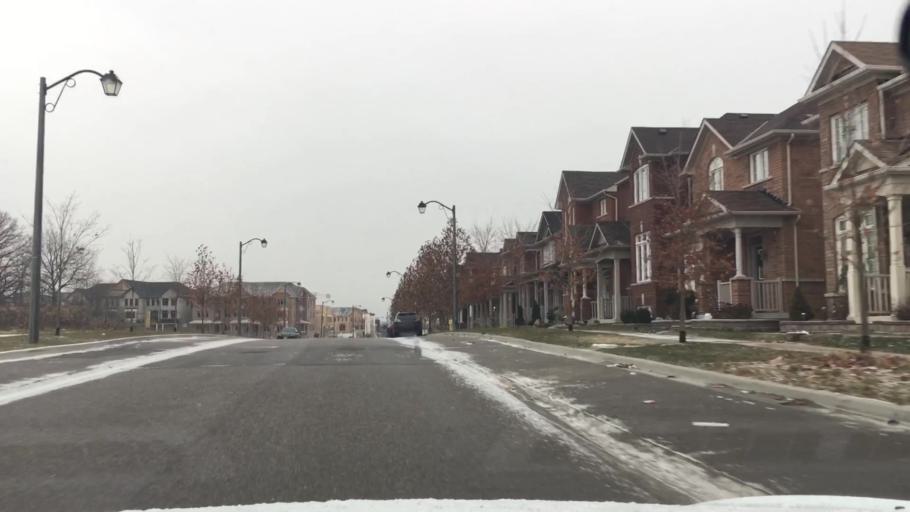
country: CA
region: Ontario
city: Markham
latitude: 43.8849
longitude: -79.2189
